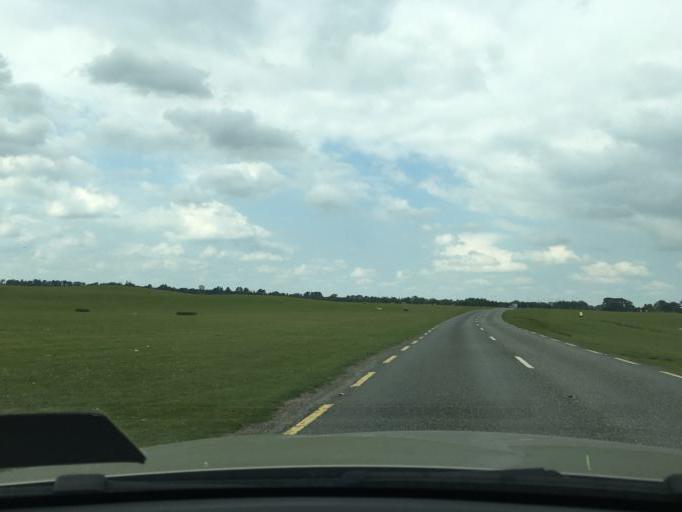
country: IE
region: Leinster
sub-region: Kildare
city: Athgarvan
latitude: 53.1556
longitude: -6.8287
